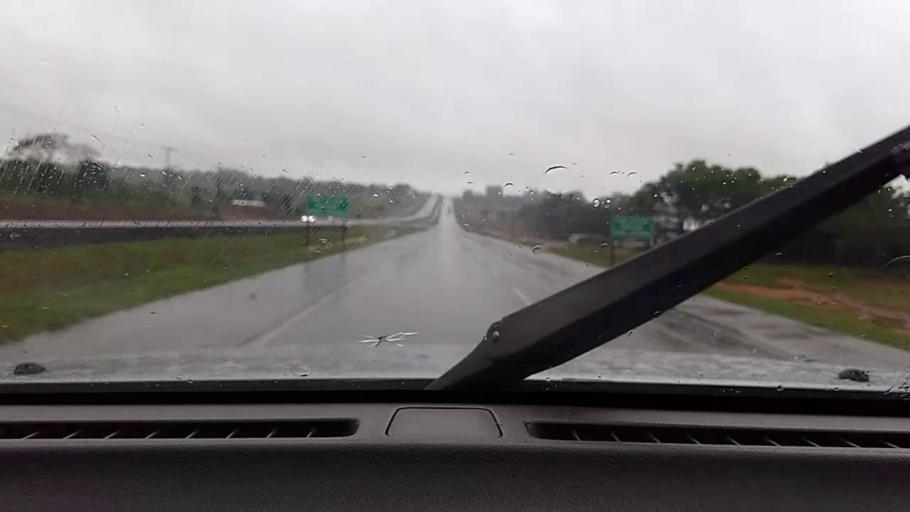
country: PY
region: Caaguazu
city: Caaguazu
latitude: -25.4657
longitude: -55.9530
